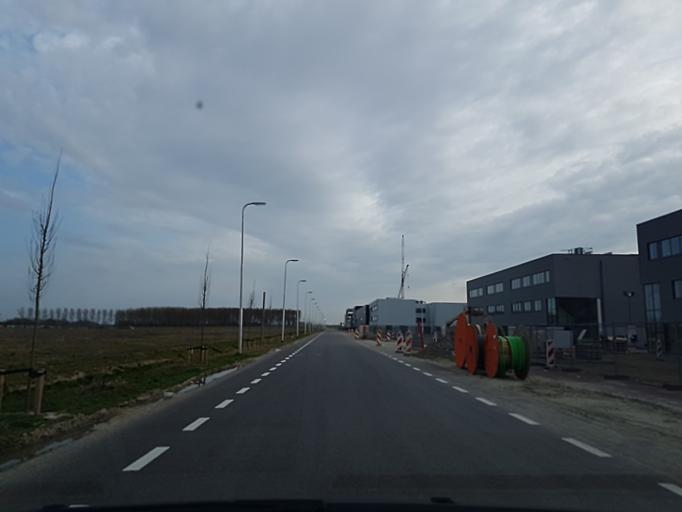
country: NL
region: Zeeland
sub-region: Gemeente Terneuzen
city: Terneuzen
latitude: 51.3410
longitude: 3.8014
